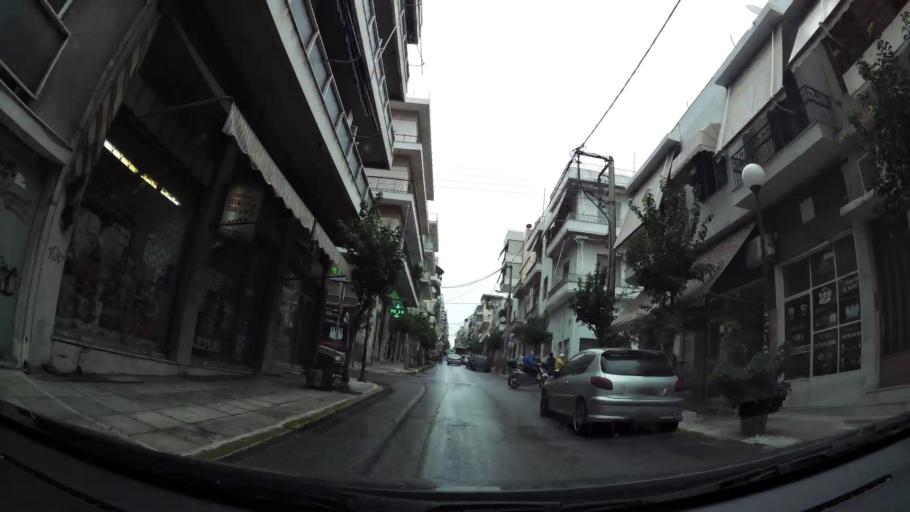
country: GR
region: Attica
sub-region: Nomos Attikis
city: Piraeus
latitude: 37.9563
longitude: 23.6423
